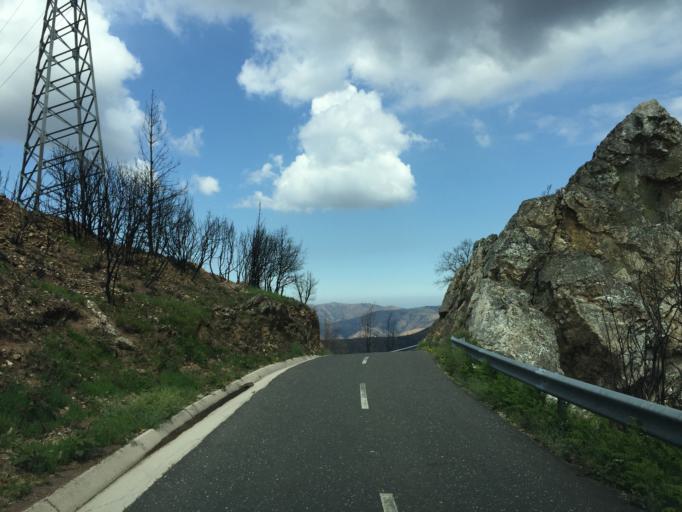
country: PT
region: Coimbra
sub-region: Pampilhosa da Serra
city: Pampilhosa da Serra
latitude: 40.1390
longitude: -7.9075
